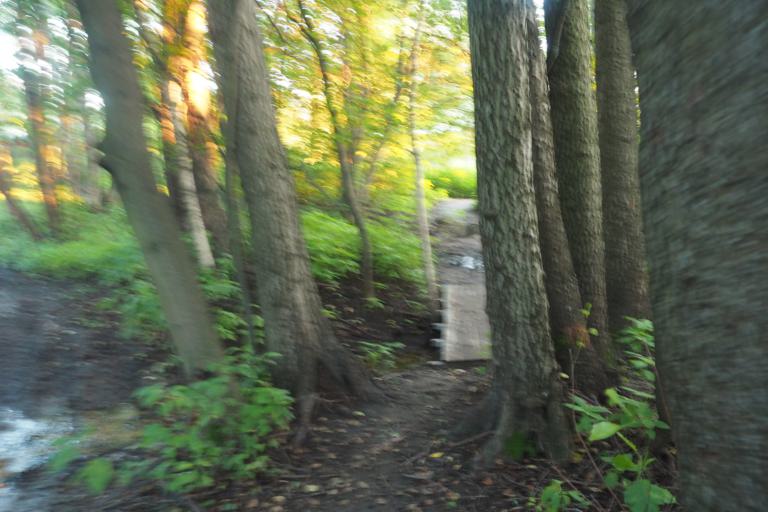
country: RU
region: Moskovskaya
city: Malyshevo
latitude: 55.5520
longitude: 38.3231
